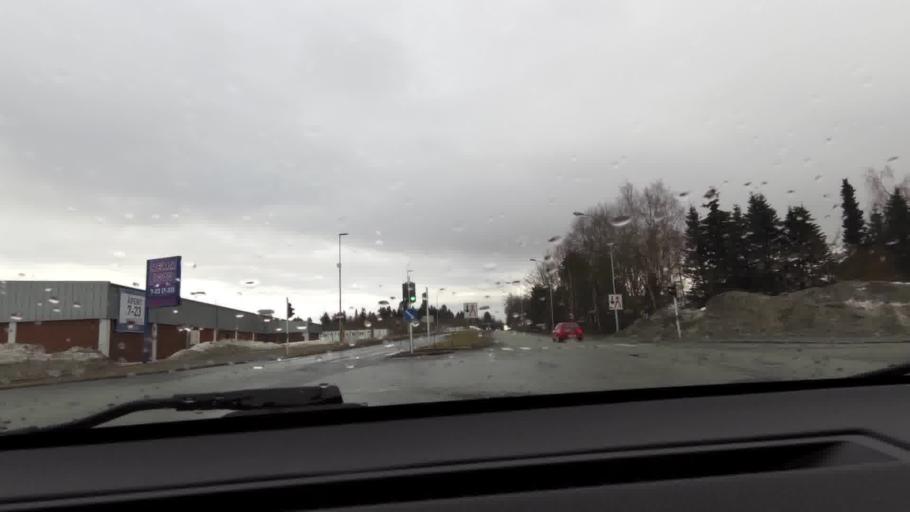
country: NO
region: Sor-Trondelag
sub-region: Trondheim
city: Trondheim
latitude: 63.3662
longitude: 10.3449
